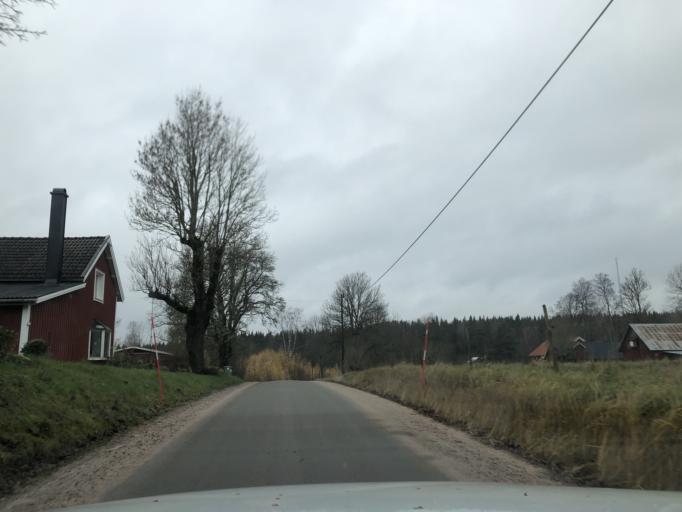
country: SE
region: Vaestra Goetaland
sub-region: Ulricehamns Kommun
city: Ulricehamn
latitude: 57.8628
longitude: 13.5719
